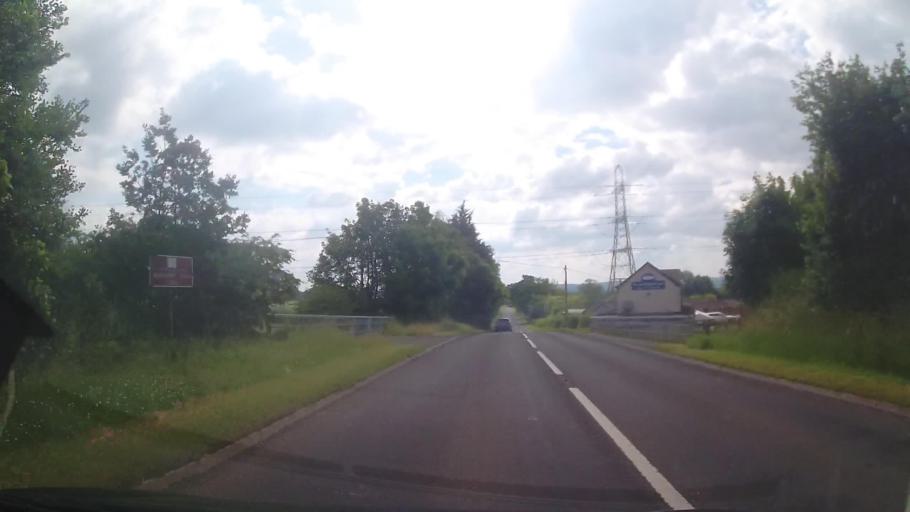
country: GB
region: England
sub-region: Shropshire
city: Whittington
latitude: 52.8867
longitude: -2.9616
